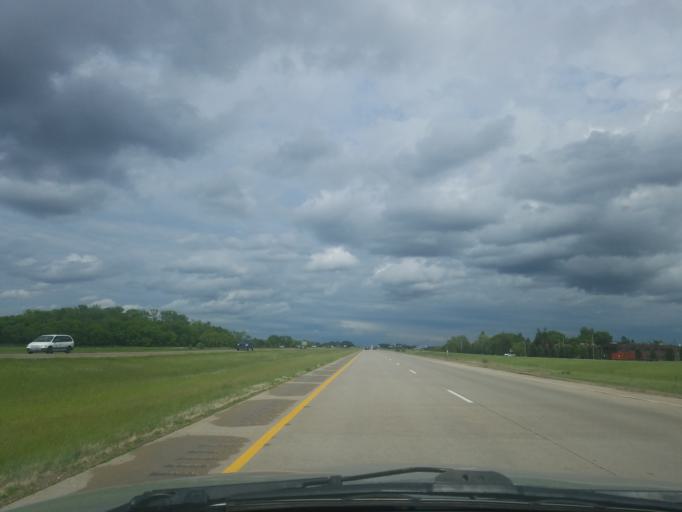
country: US
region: North Dakota
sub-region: Cass County
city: West Fargo
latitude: 46.8774
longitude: -97.0038
